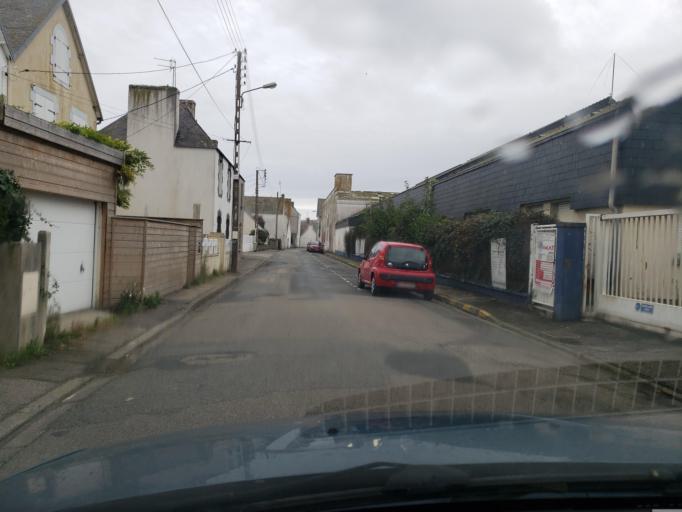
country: FR
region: Brittany
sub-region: Departement du Finistere
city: Guilvinec
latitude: 47.7989
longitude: -4.2834
